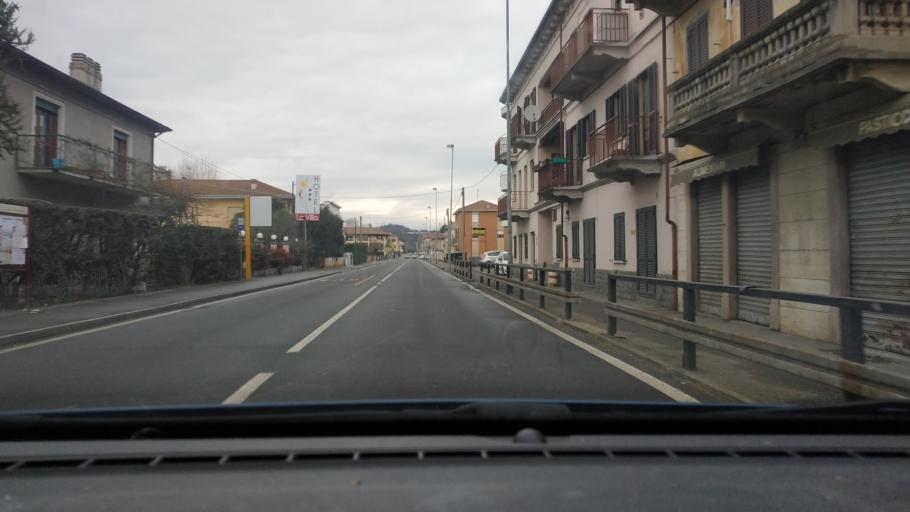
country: IT
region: Piedmont
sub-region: Provincia di Torino
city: Pavone Canavese
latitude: 45.4352
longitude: 7.8799
